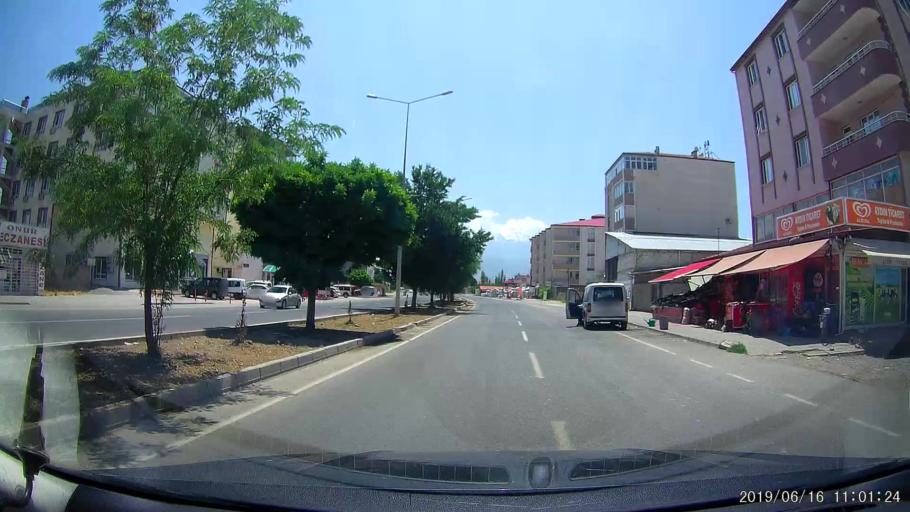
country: TR
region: Igdir
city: Igdir
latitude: 39.9152
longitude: 44.0495
